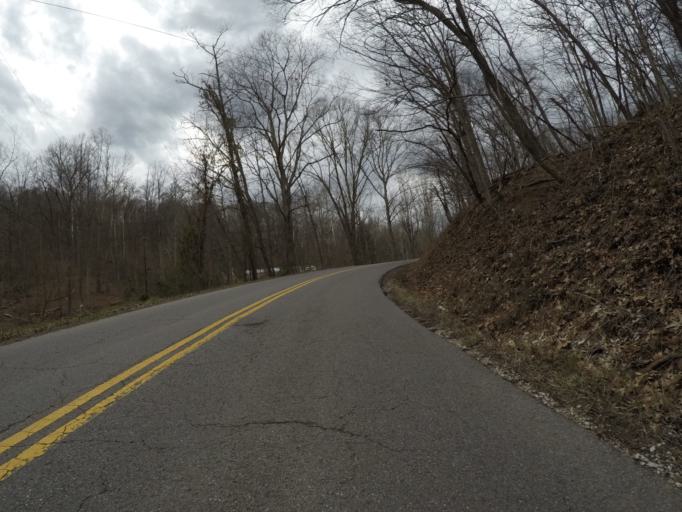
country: US
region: Ohio
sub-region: Lawrence County
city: Burlington
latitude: 38.4291
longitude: -82.5243
